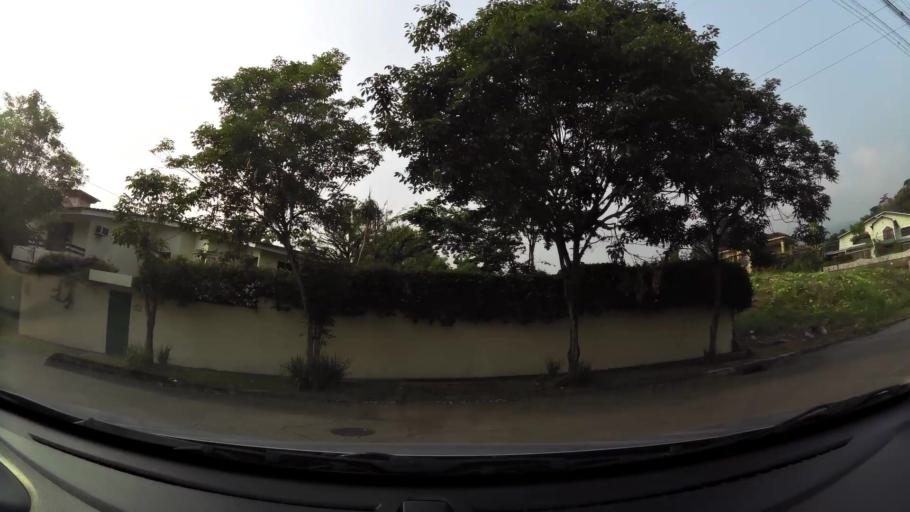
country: HN
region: Cortes
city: Armenta
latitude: 15.4926
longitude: -88.0477
